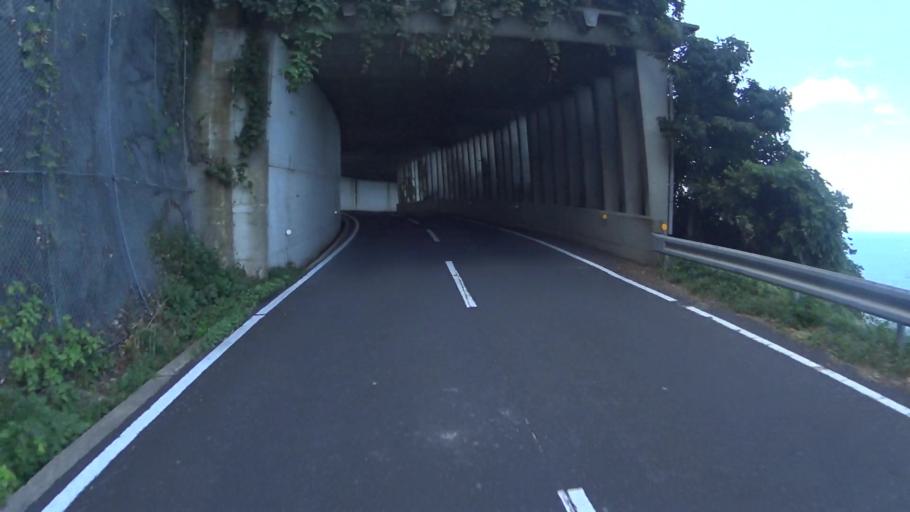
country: JP
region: Kyoto
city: Miyazu
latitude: 35.7595
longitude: 135.2433
